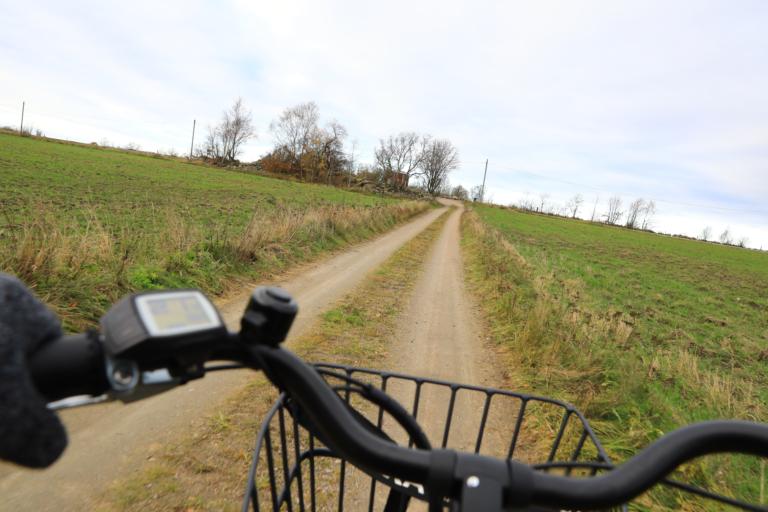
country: SE
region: Halland
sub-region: Varbergs Kommun
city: Traslovslage
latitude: 57.0603
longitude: 12.3254
